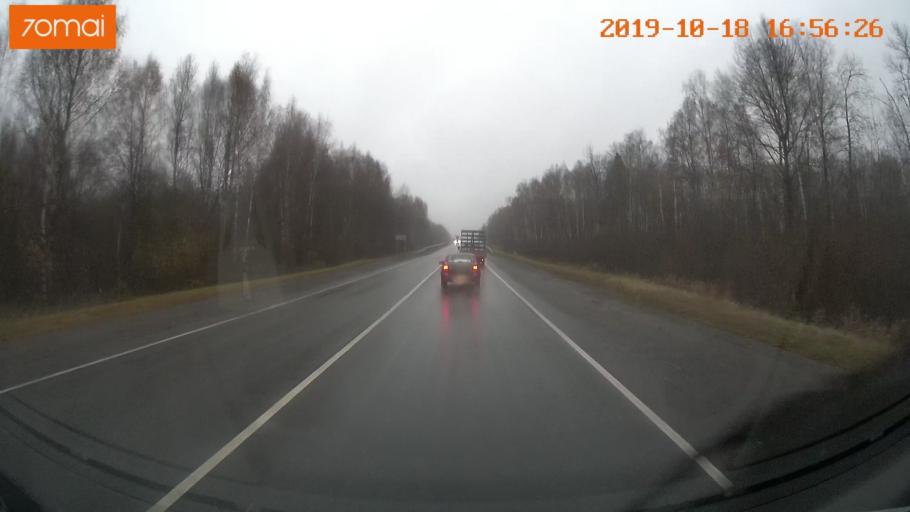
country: RU
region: Ivanovo
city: Novoye Leushino
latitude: 56.6569
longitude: 40.5881
